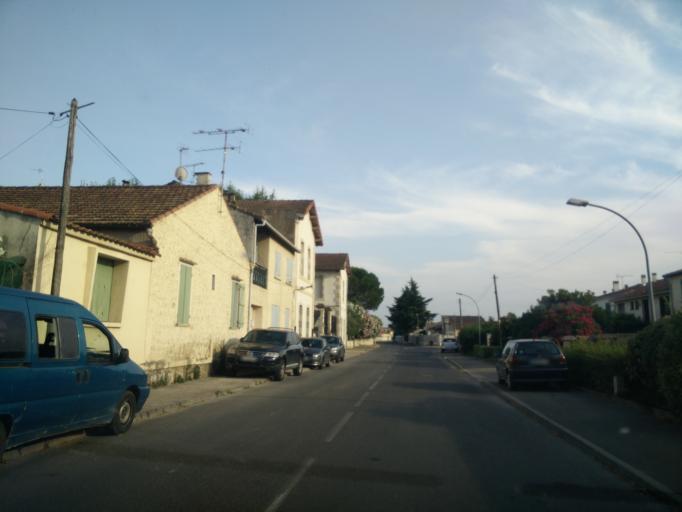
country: FR
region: Languedoc-Roussillon
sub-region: Departement de l'Herault
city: Marsillargues
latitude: 43.6629
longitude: 4.1712
